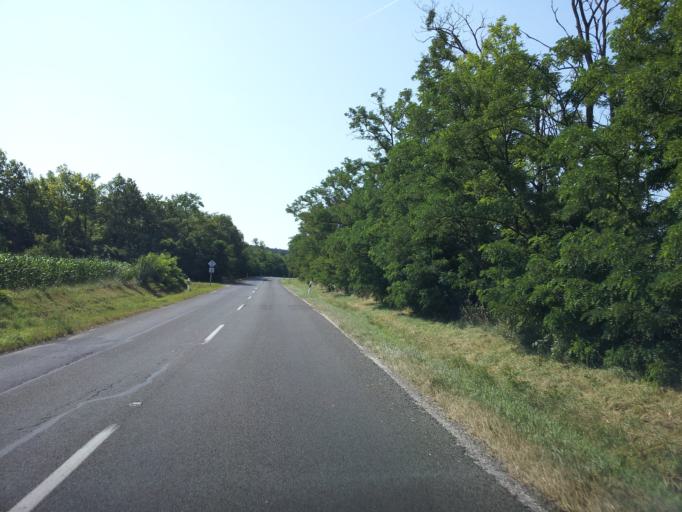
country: HU
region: Fejer
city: Lovasbereny
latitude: 47.2747
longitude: 18.5257
